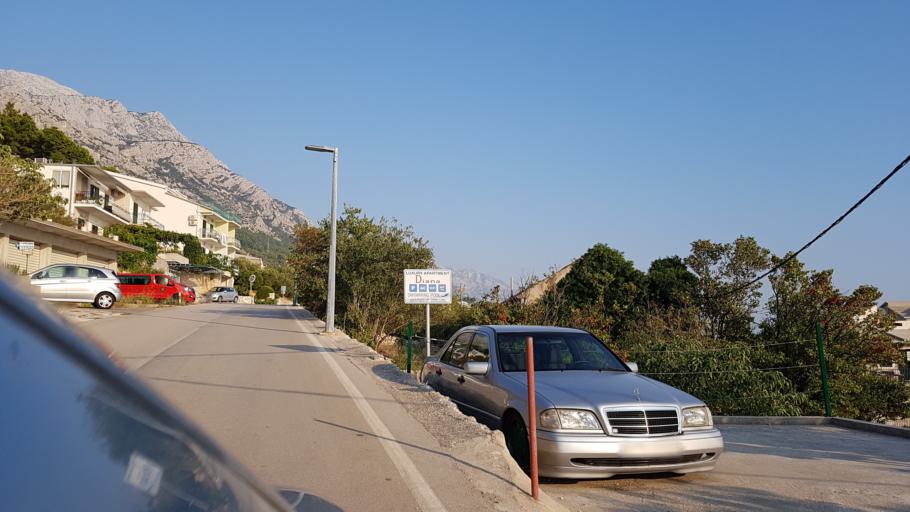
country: HR
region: Splitsko-Dalmatinska
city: Donja Brela
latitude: 43.3835
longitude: 16.9102
